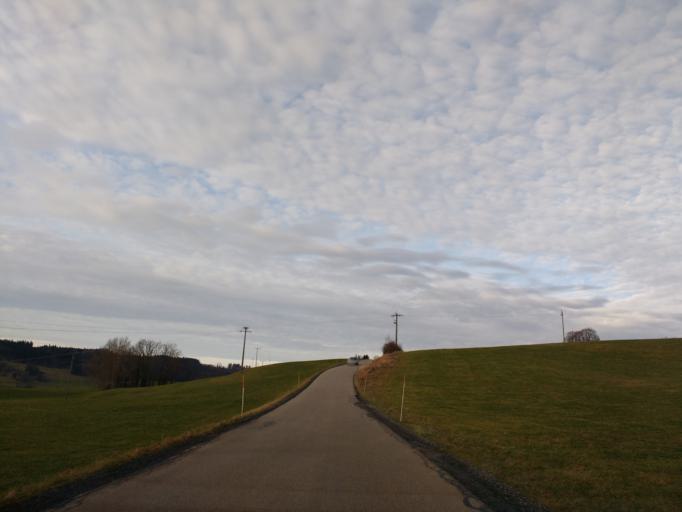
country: DE
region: Bavaria
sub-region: Swabia
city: Wildpoldsried
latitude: 47.7850
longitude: 10.4088
